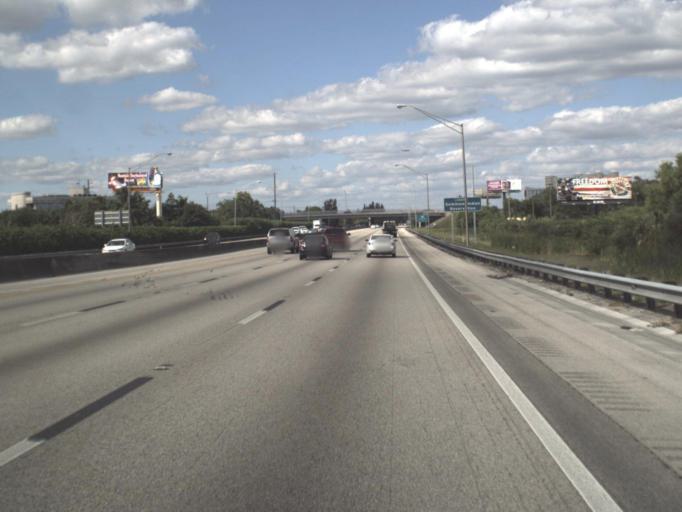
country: US
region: Florida
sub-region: Broward County
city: Davie
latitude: 26.0421
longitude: -80.2141
